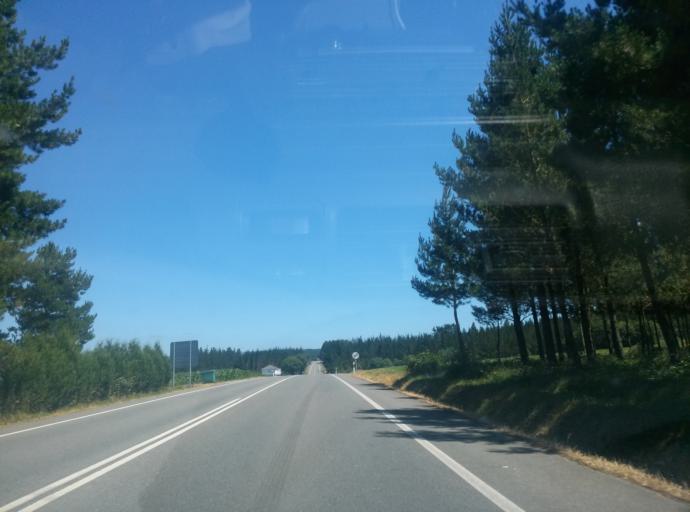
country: ES
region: Galicia
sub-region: Provincia de Lugo
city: Castro de Rei
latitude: 43.2346
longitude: -7.3926
